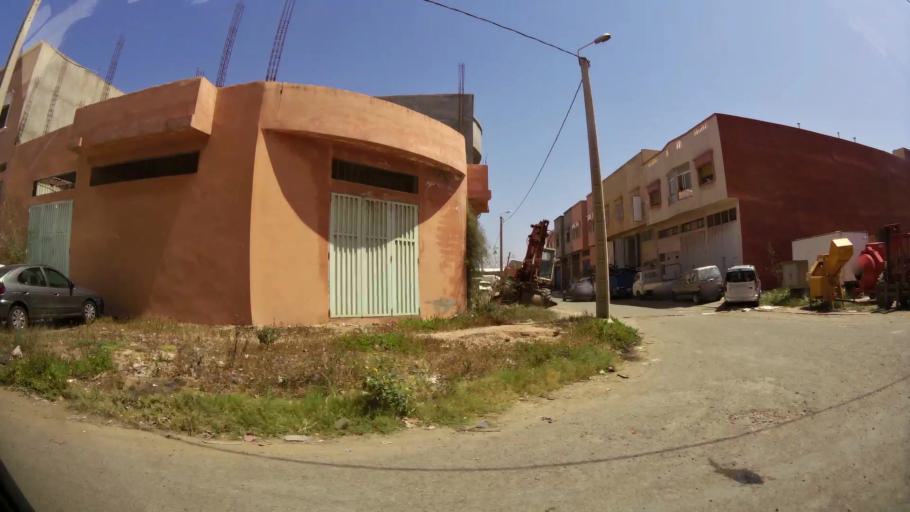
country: MA
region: Souss-Massa-Draa
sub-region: Inezgane-Ait Mellou
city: Inezgane
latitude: 30.3367
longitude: -9.4812
